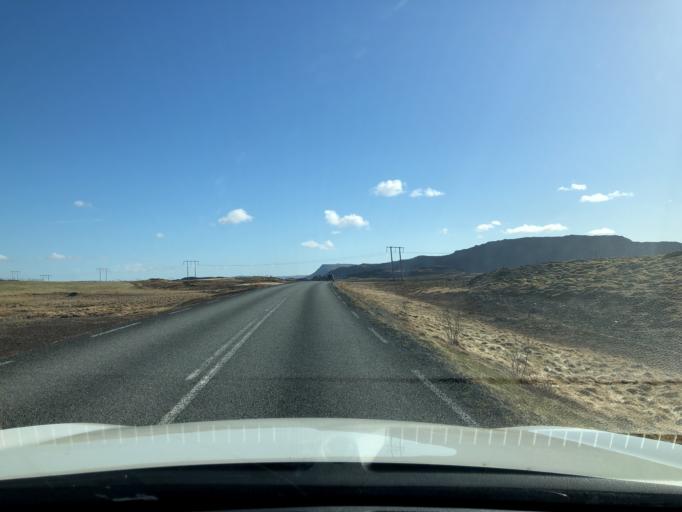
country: IS
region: West
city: Borgarnes
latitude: 64.5608
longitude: -21.7154
